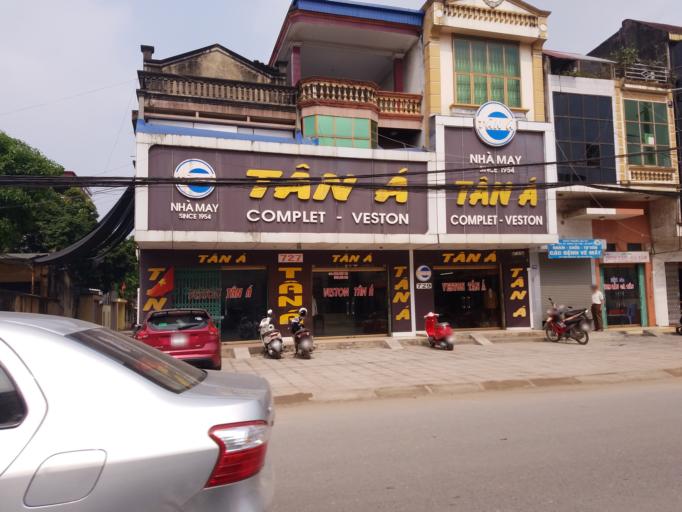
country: VN
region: Thai Nguyen
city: Thanh Pho Thai Nguyen
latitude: 21.5797
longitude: 105.8384
